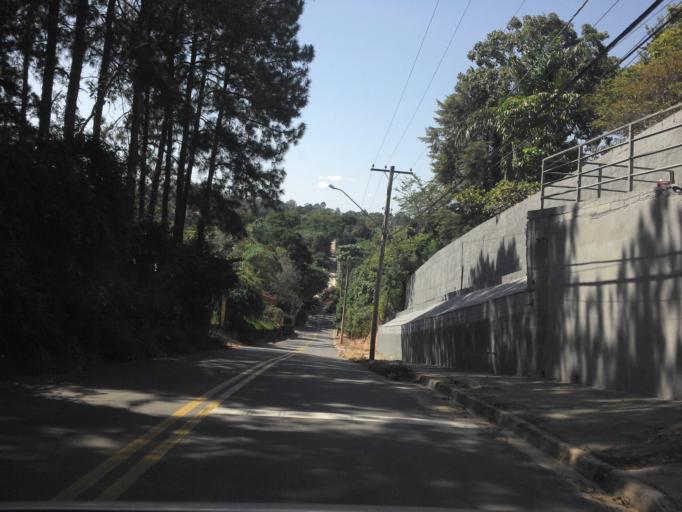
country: BR
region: Sao Paulo
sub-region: Vinhedo
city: Vinhedo
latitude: -23.0103
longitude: -47.0137
